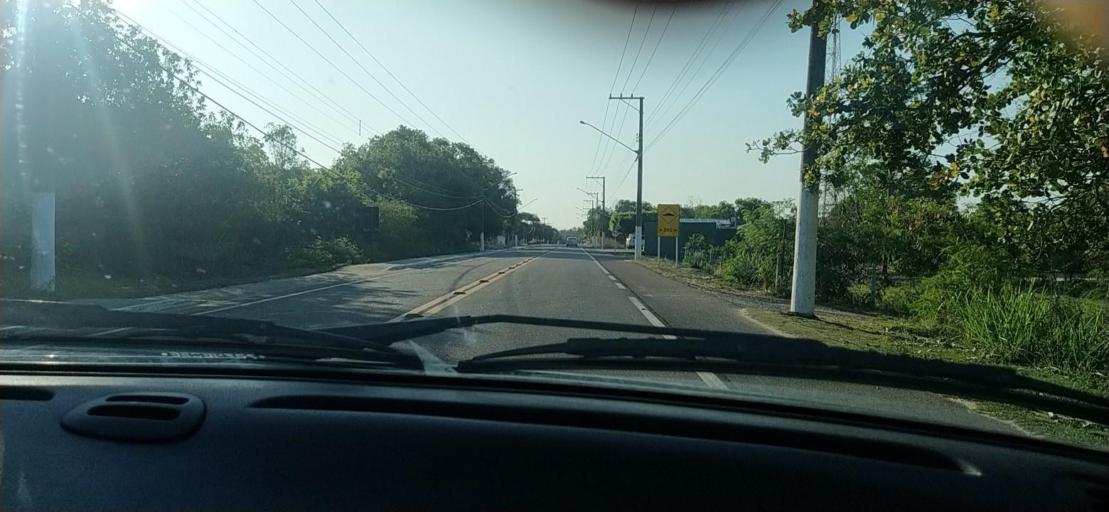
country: BR
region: Espirito Santo
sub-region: Conceicao Da Barra
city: Conceicao da Barra
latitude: -18.5721
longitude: -39.7373
